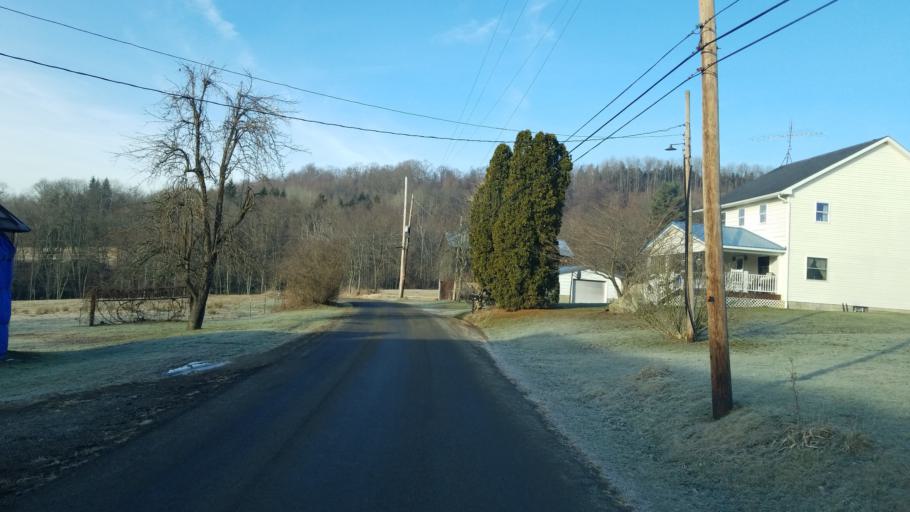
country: US
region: Pennsylvania
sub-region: Jefferson County
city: Brookville
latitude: 40.9581
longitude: -79.2619
